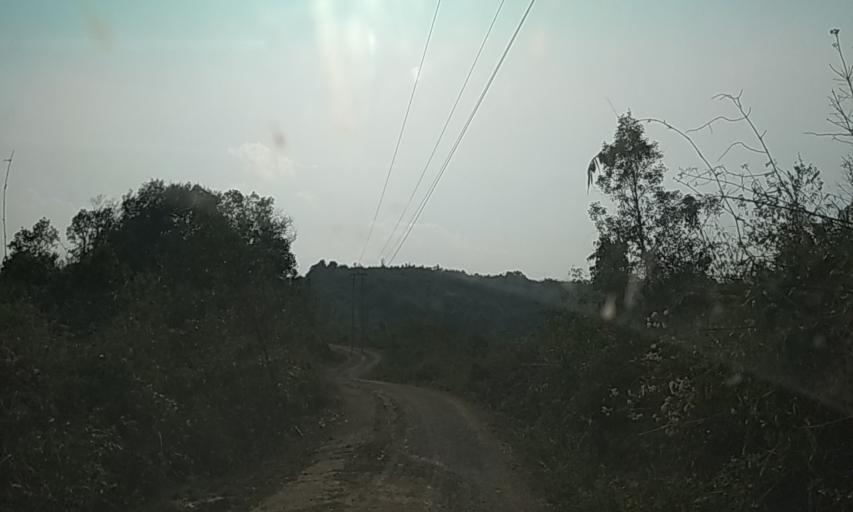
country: LA
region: Louangphabang
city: Louangphabang
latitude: 20.0378
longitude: 101.8274
